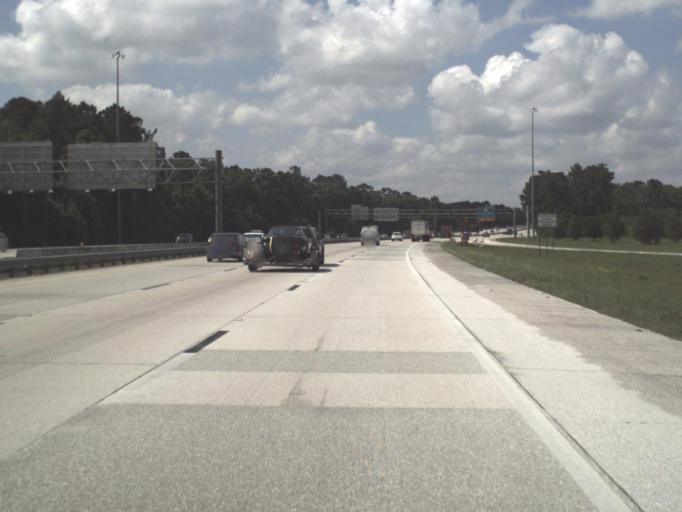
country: US
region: Florida
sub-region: Saint Johns County
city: Fruit Cove
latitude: 30.1750
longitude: -81.5585
